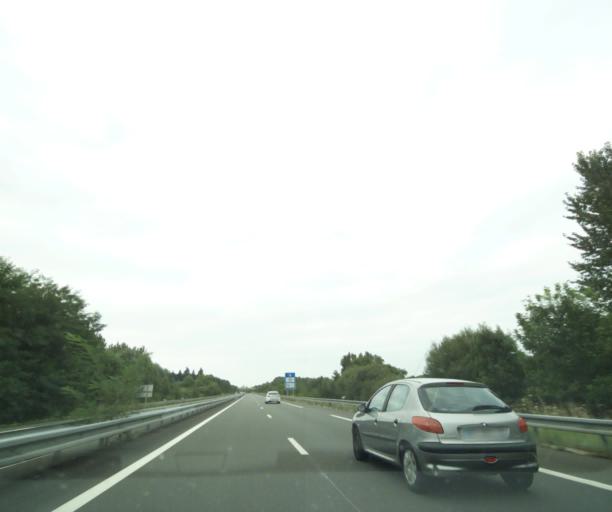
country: FR
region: Pays de la Loire
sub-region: Departement de la Sarthe
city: Ecommoy
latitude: 47.8332
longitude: 0.3061
